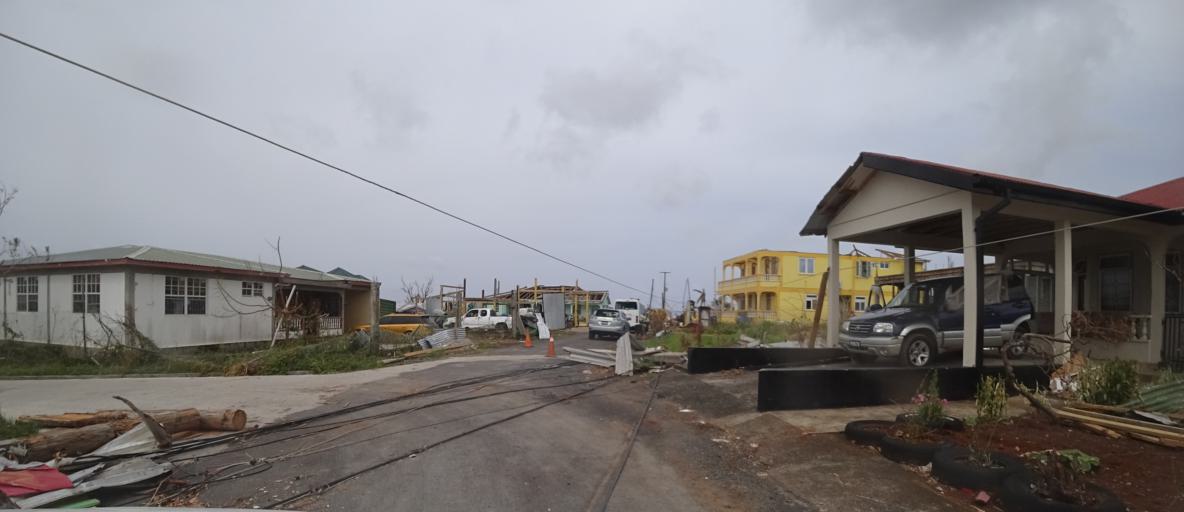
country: DM
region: Saint Andrew
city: Calibishie
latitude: 15.5913
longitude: -61.3981
